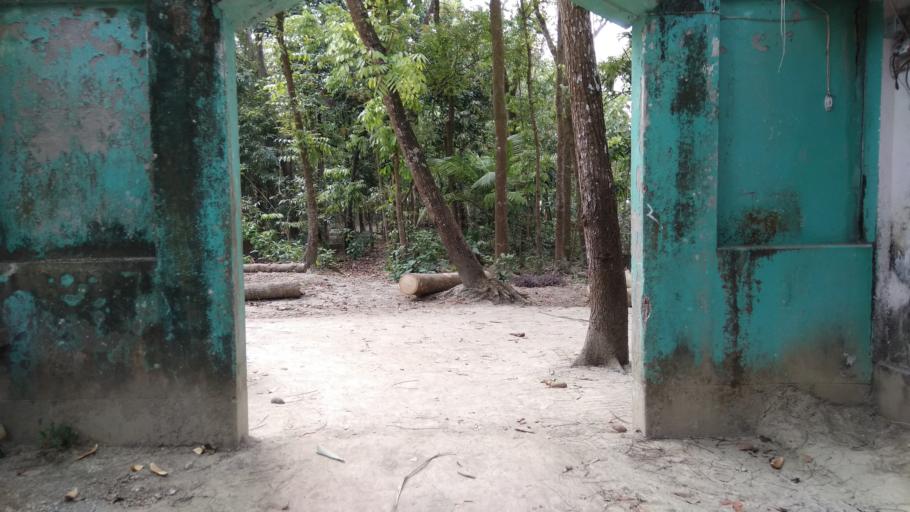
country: BD
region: Barisal
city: Mehendiganj
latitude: 22.9377
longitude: 90.4137
